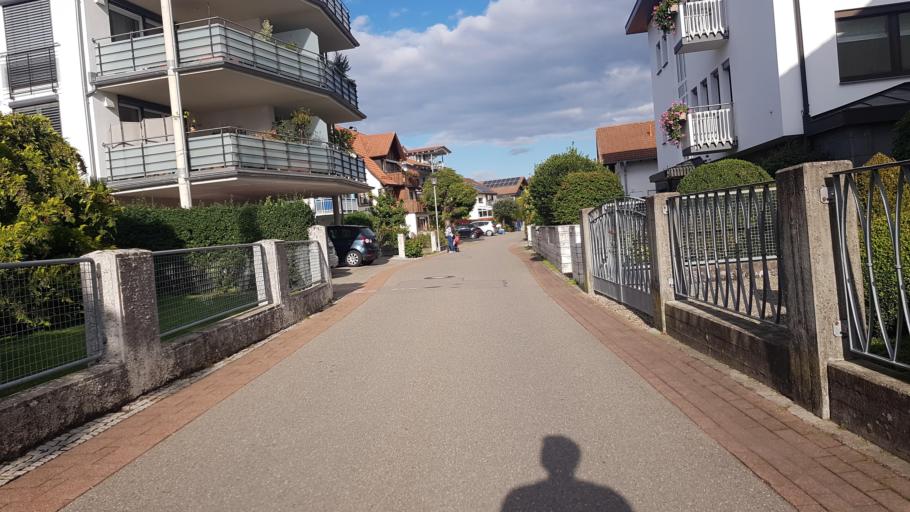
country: DE
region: Baden-Wuerttemberg
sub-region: Tuebingen Region
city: Immenstaad am Bodensee
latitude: 47.6648
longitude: 9.3678
